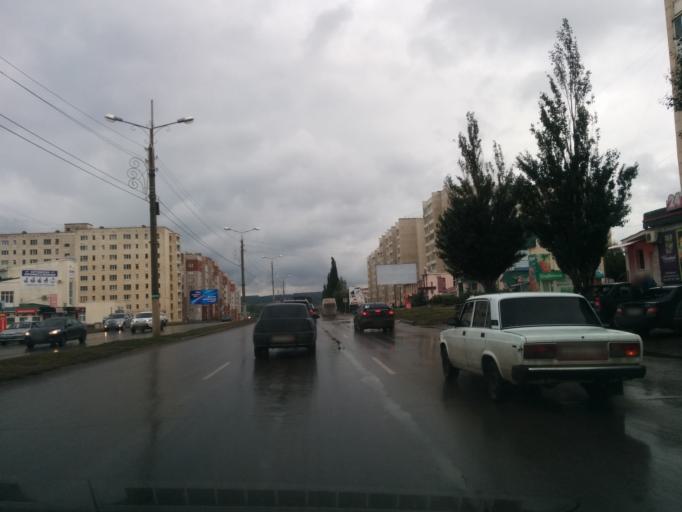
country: RU
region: Bashkortostan
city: Oktyabr'skiy
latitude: 54.4819
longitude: 53.5162
